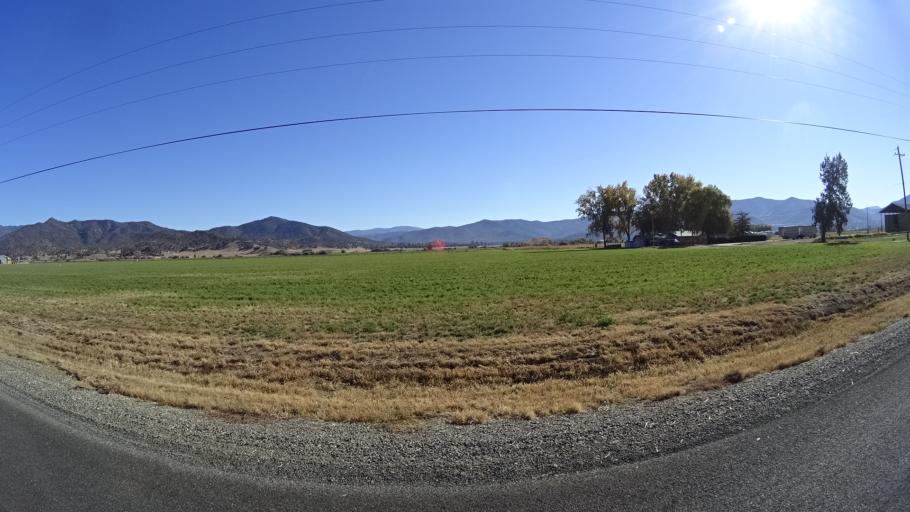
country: US
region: California
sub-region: Siskiyou County
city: Yreka
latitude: 41.5731
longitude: -122.8552
